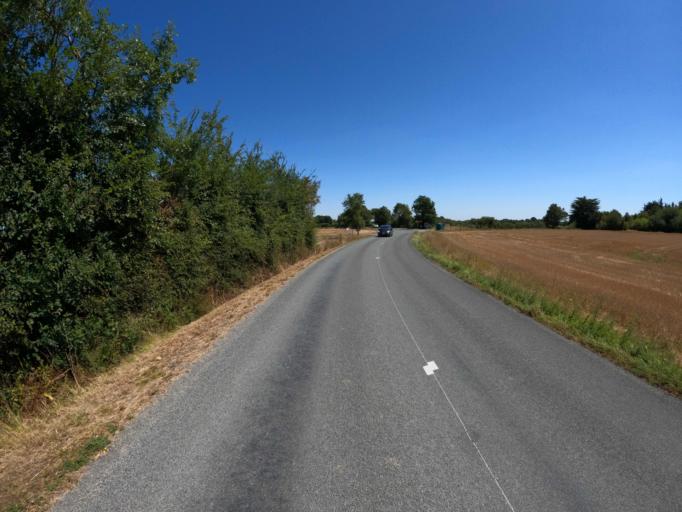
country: FR
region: Pays de la Loire
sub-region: Departement de la Vendee
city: Saint-Philbert-de-Bouaine
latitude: 46.9761
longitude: -1.5464
